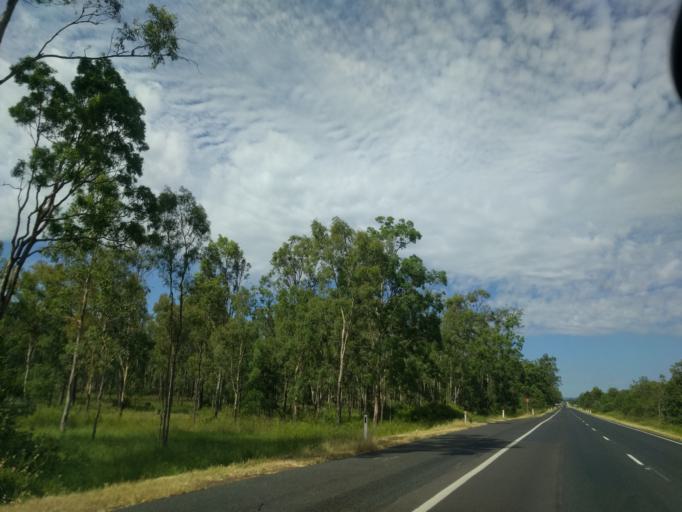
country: AU
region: Queensland
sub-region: Lockyer Valley
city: Gatton
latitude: -27.5378
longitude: 152.2483
